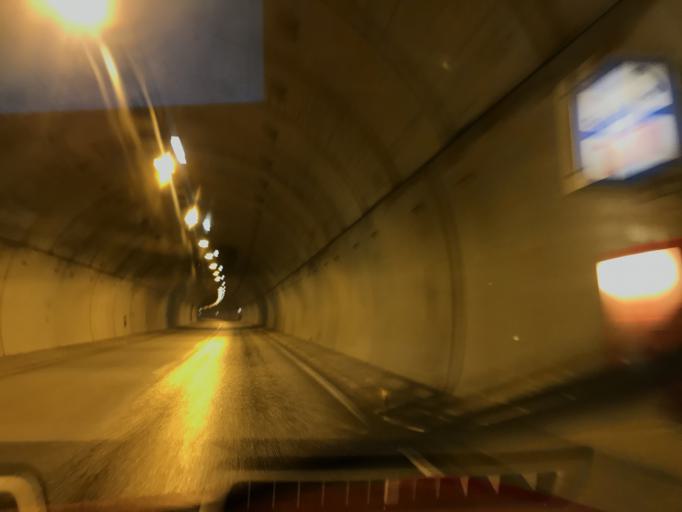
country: NO
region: Aust-Agder
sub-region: Lillesand
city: Lillesand
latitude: 58.2653
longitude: 8.3354
